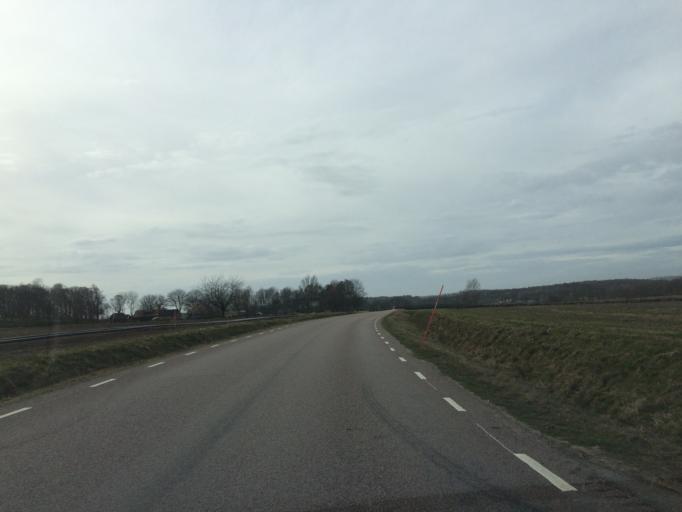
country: SE
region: Halland
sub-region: Halmstads Kommun
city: Getinge
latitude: 56.8582
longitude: 12.6500
